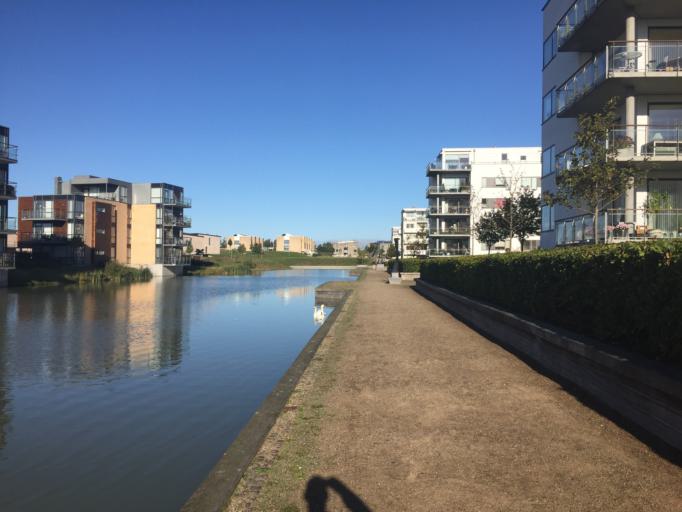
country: DK
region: Capital Region
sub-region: Ballerup Kommune
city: Malov
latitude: 55.7454
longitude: 12.3190
